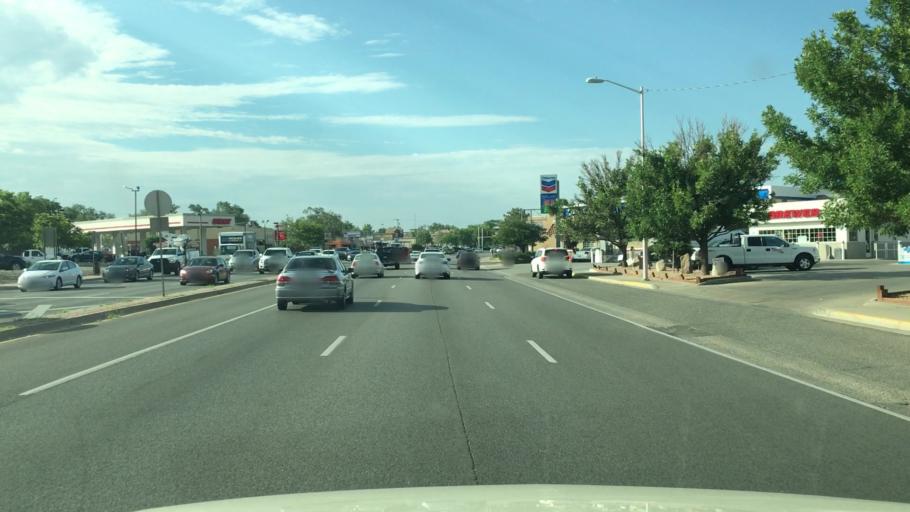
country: US
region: New Mexico
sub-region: Santa Fe County
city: Santa Fe
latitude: 35.6771
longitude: -105.9539
